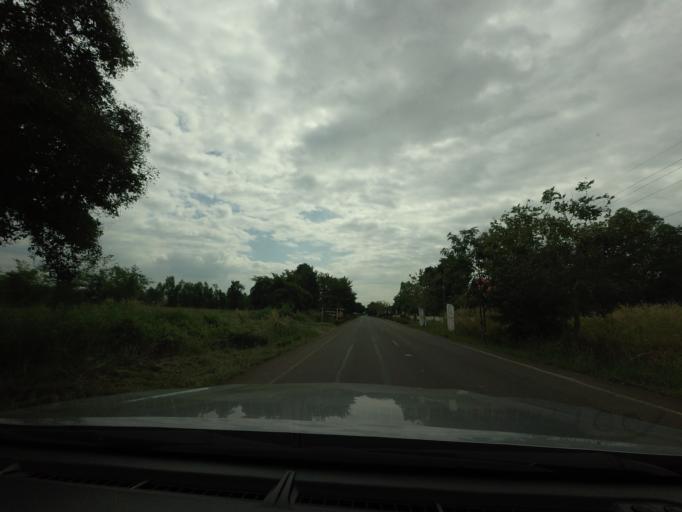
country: TH
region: Phitsanulok
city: Noen Maprang
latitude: 16.6210
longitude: 100.6189
